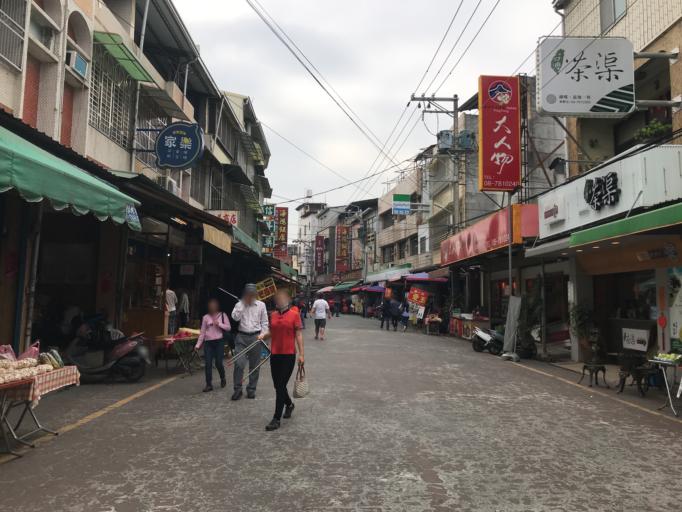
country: TW
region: Taiwan
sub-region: Pingtung
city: Pingtung
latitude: 22.5748
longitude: 120.5691
